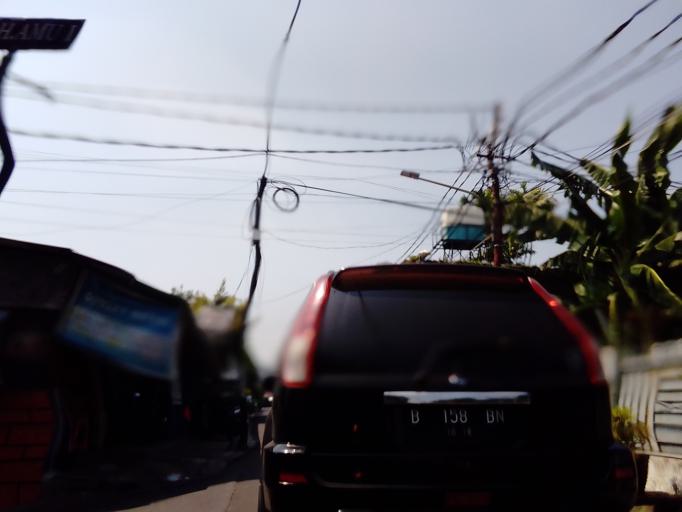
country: ID
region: Jakarta Raya
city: Jakarta
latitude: -6.2615
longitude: 106.8031
